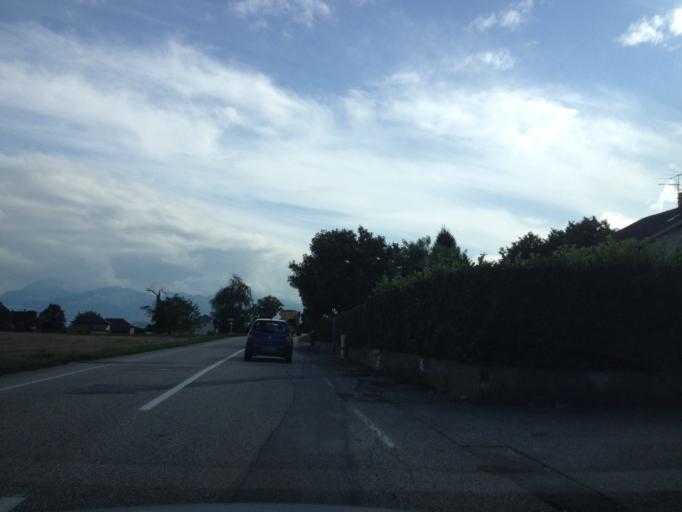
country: FR
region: Rhone-Alpes
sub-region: Departement de la Savoie
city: Le Bourget-du-Lac
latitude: 45.6349
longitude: 5.8629
